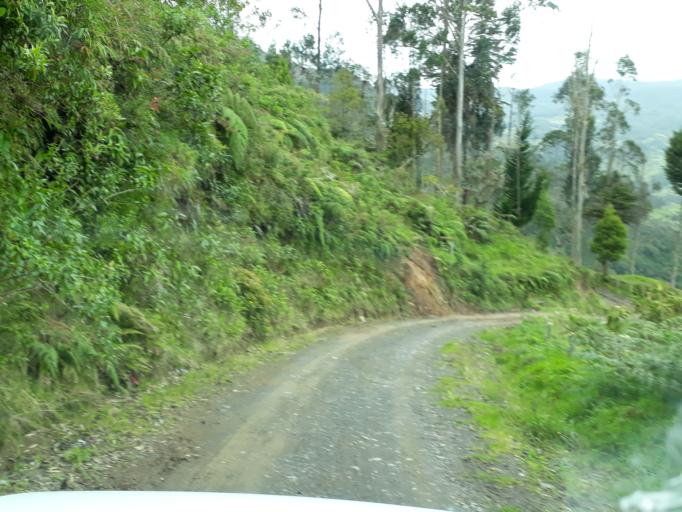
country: CO
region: Cundinamarca
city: Junin
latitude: 4.7450
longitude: -73.6287
